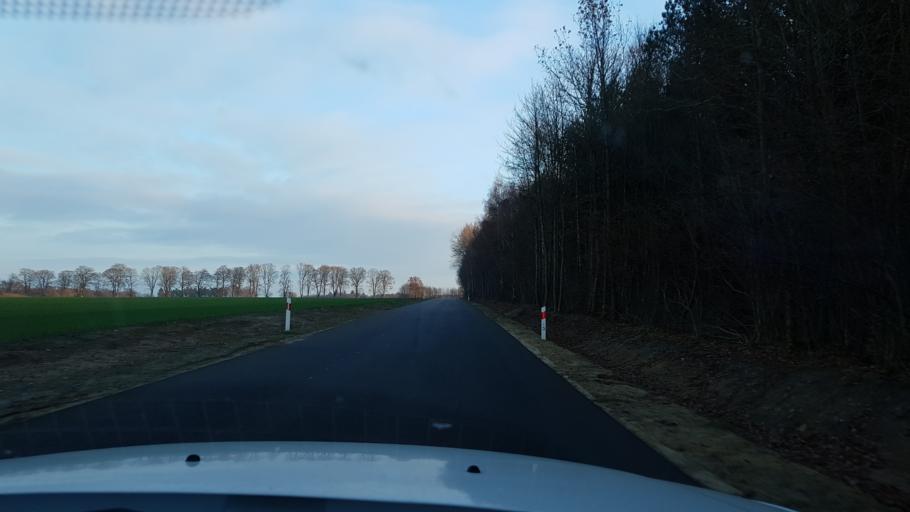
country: PL
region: West Pomeranian Voivodeship
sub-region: Koszalin
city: Koszalin
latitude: 54.1179
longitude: 16.1129
